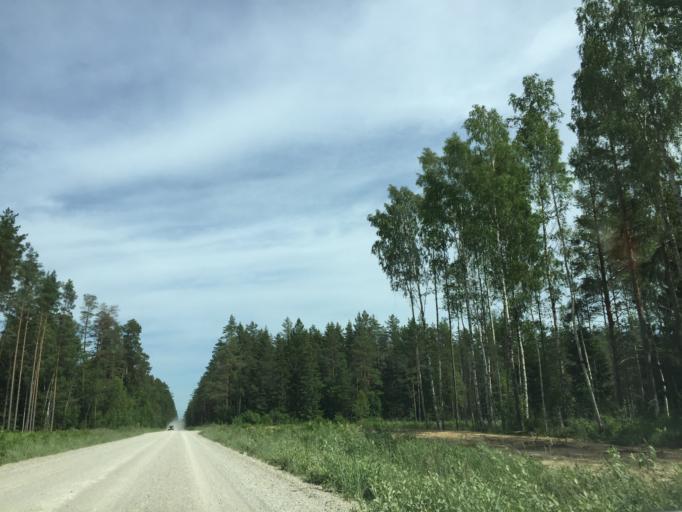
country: LV
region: Dundaga
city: Dundaga
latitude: 57.6176
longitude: 22.5287
